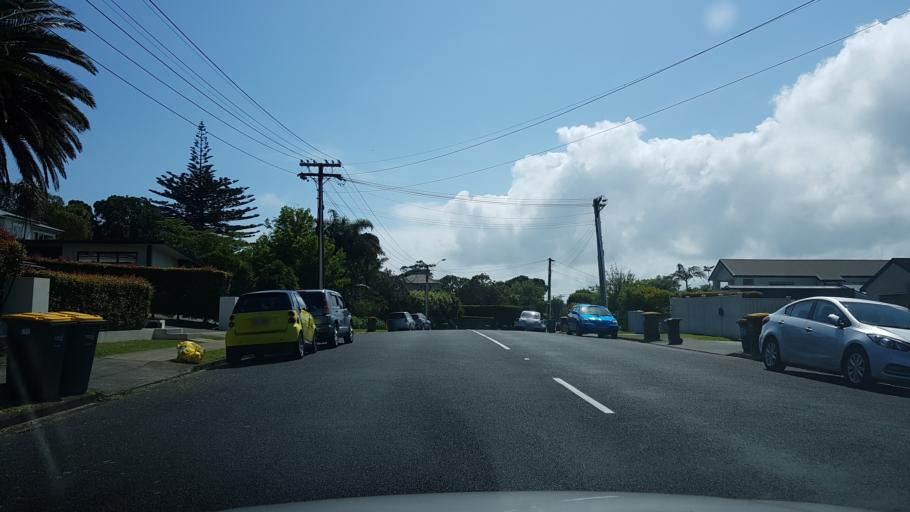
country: NZ
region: Auckland
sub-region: Auckland
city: North Shore
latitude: -36.8075
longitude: 174.7922
